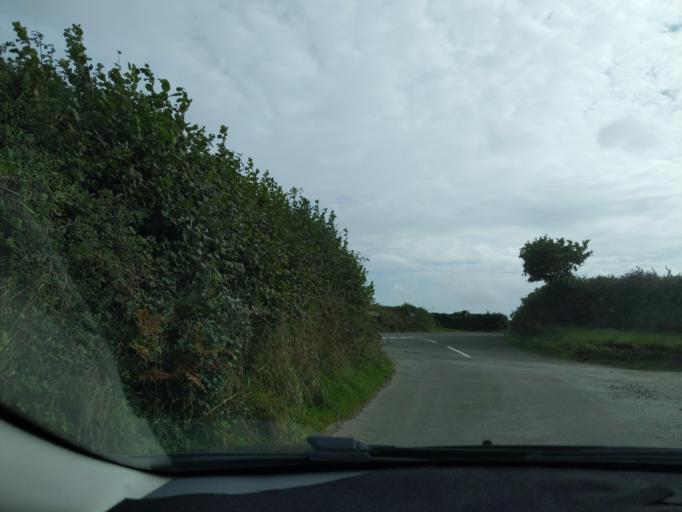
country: GB
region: England
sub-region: Cornwall
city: Mevagissey
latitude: 50.2772
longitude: -4.8301
